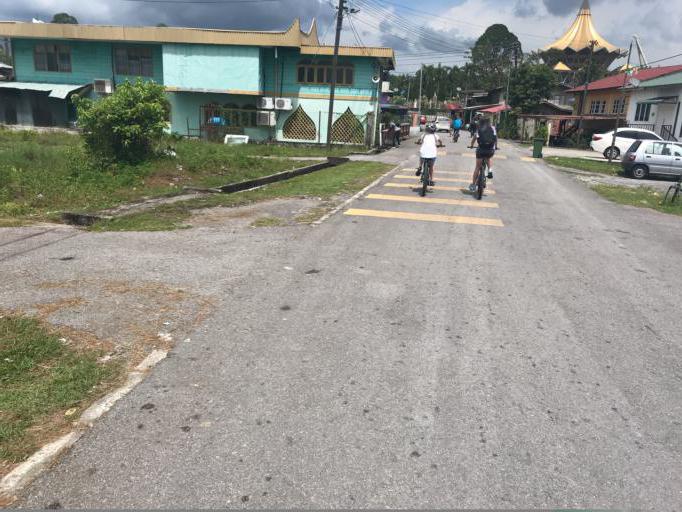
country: MY
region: Sarawak
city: Kuching
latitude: 1.5634
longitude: 110.3433
